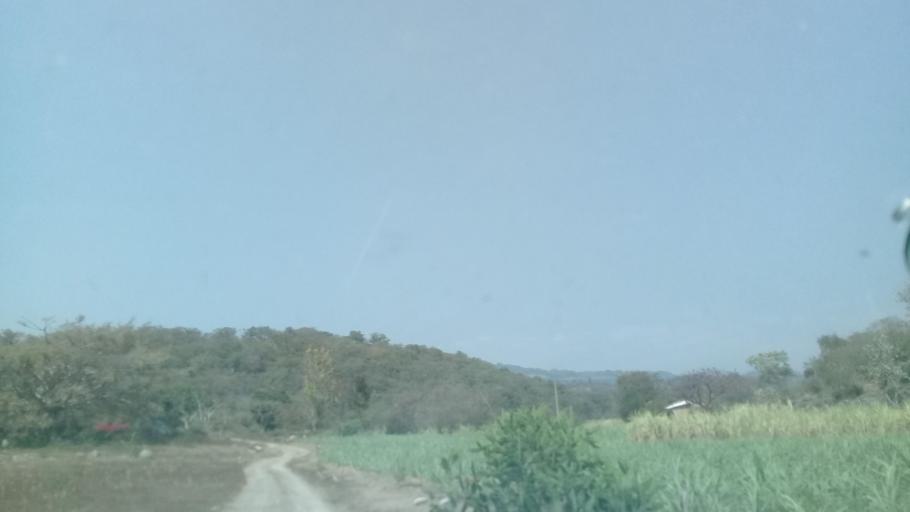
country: MX
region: Veracruz
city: El Castillo
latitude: 19.5689
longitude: -96.8068
